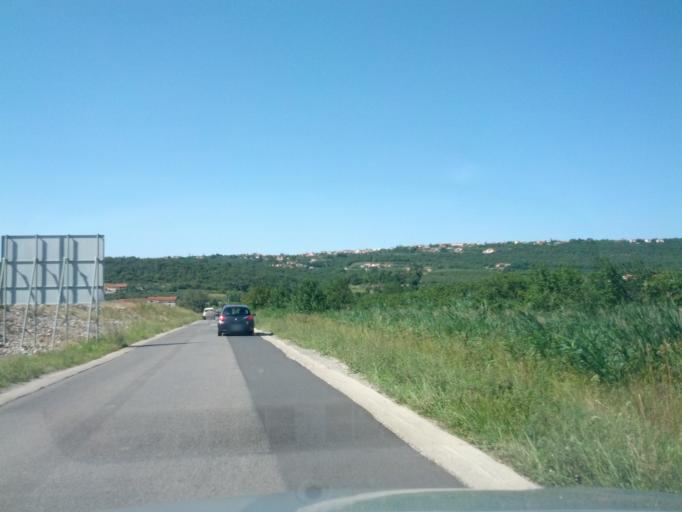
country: SI
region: Koper-Capodistria
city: Hrvatini
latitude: 45.5633
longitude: 13.7582
